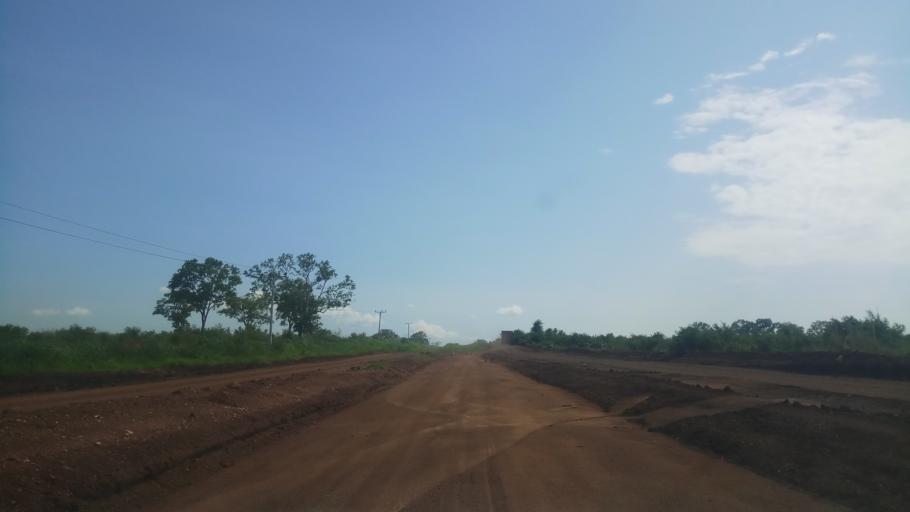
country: ET
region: Gambela
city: Gambela
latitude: 8.1809
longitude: 34.4933
